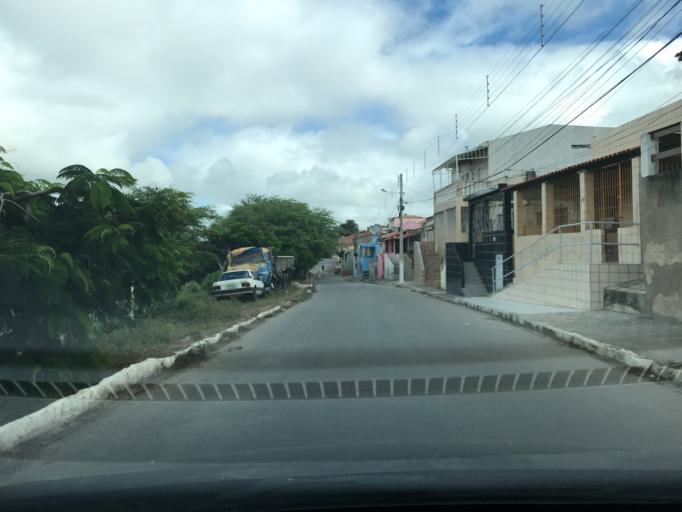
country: BR
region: Pernambuco
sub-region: Bezerros
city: Bezerros
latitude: -8.2335
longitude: -35.7555
